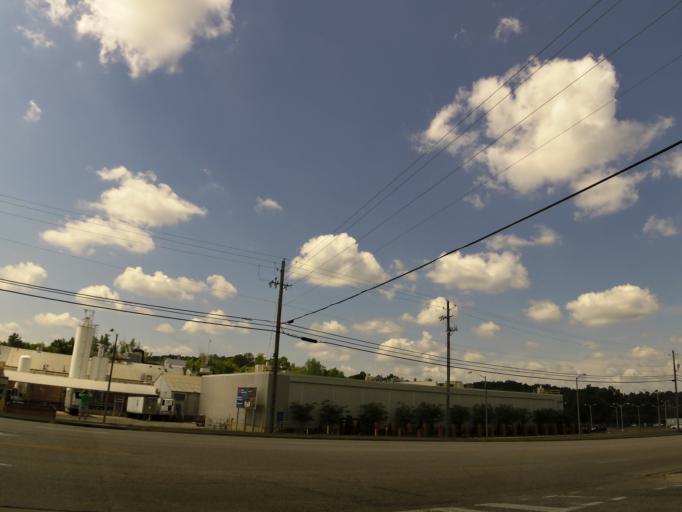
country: US
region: Alabama
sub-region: Marion County
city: Guin
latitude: 33.9669
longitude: -87.9000
